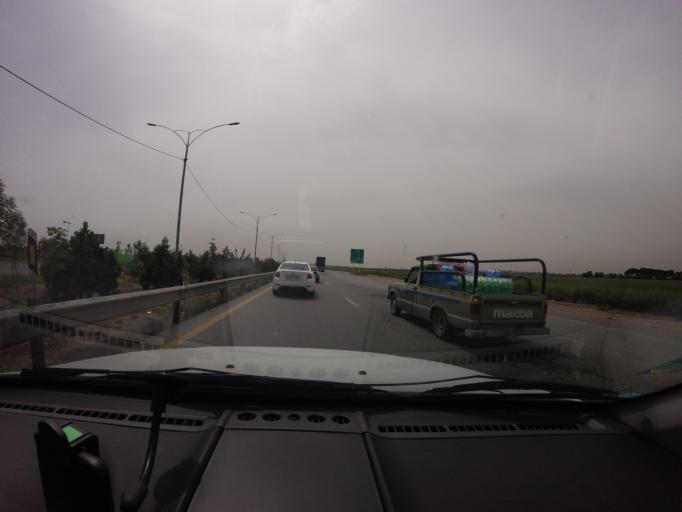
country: IR
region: Tehran
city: Eslamshahr
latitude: 35.5918
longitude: 51.2422
